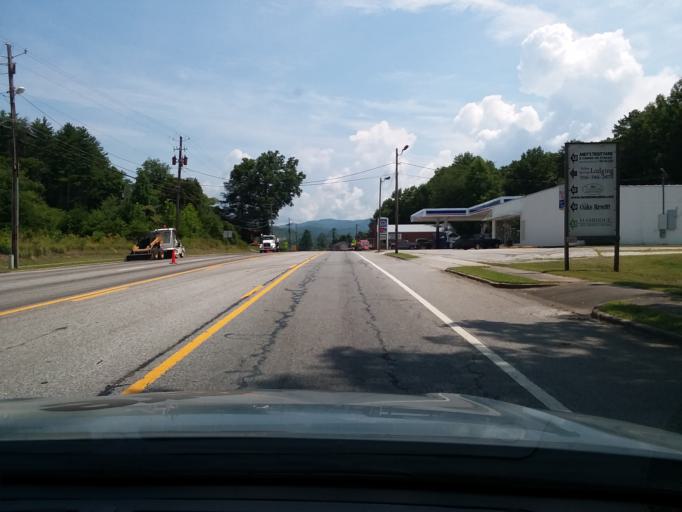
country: US
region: Georgia
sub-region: Rabun County
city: Mountain City
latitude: 34.9704
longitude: -83.3869
